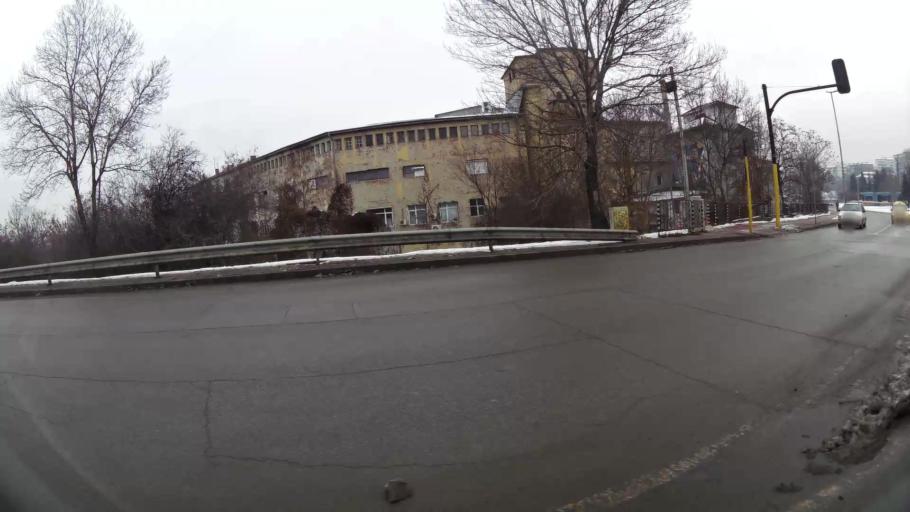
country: BG
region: Sofia-Capital
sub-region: Stolichna Obshtina
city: Sofia
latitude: 42.7156
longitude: 23.3100
